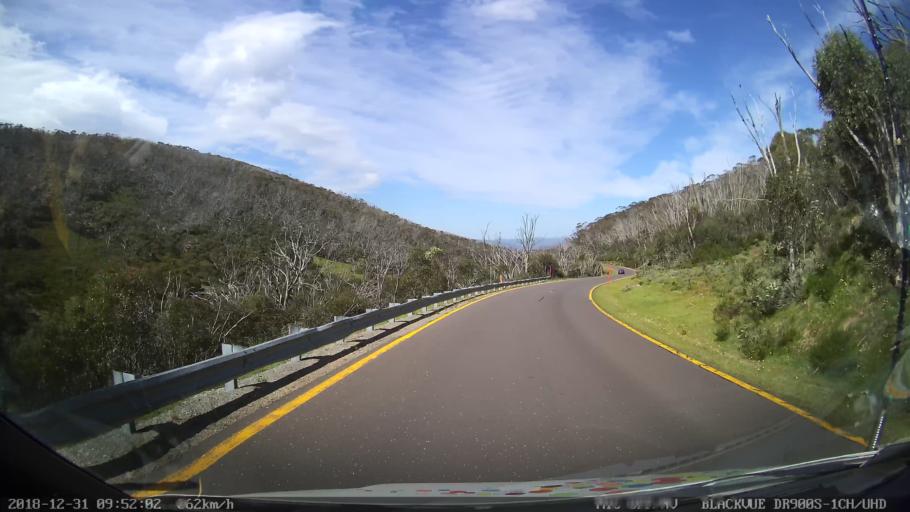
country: AU
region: New South Wales
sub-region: Snowy River
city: Jindabyne
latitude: -36.5251
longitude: 148.2572
